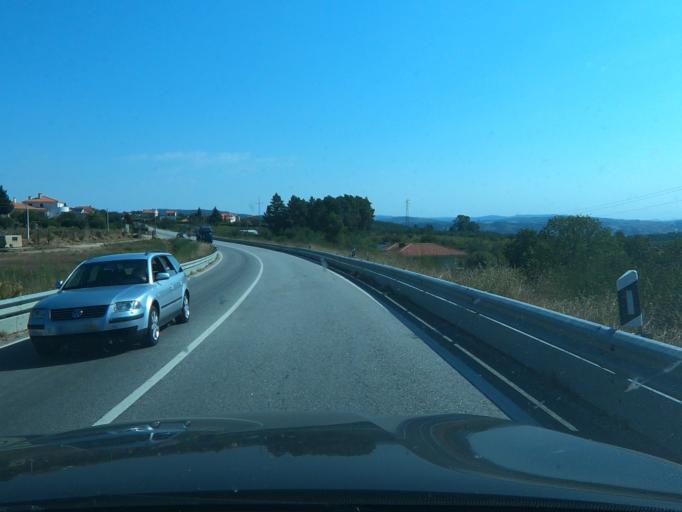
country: PT
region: Vila Real
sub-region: Sabrosa
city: Sabrosa
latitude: 41.2614
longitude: -7.6035
